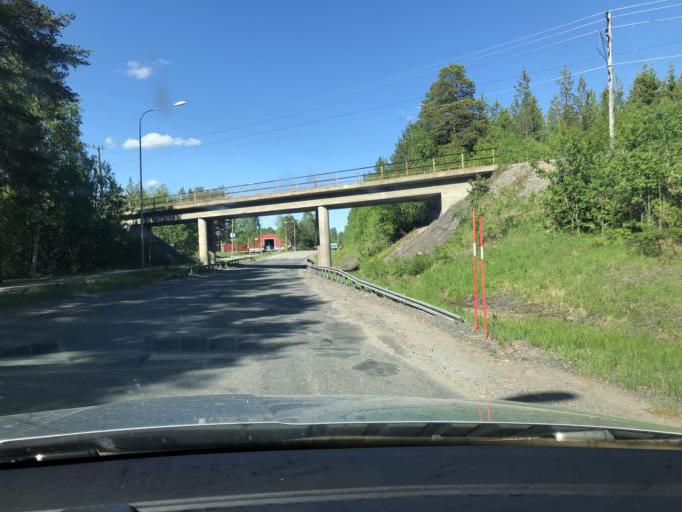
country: SE
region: Norrbotten
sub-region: Kalix Kommun
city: Kalix
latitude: 65.8658
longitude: 23.1406
